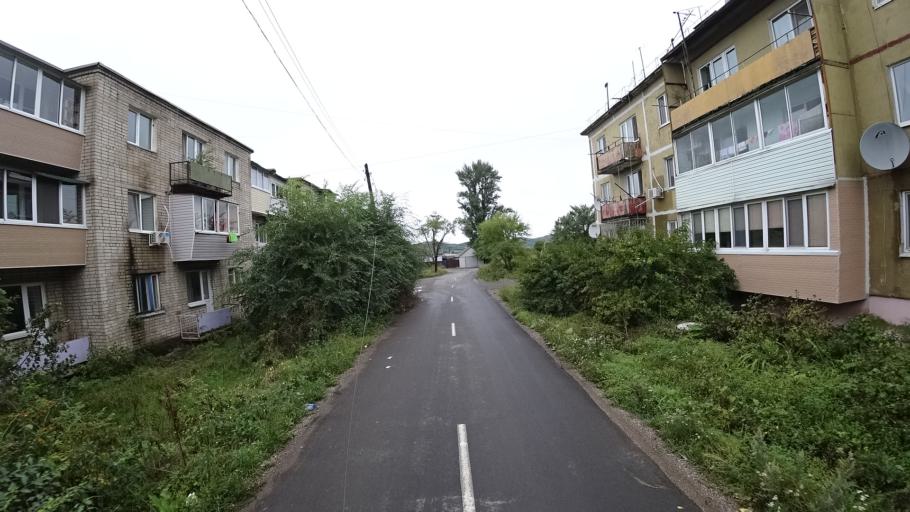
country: RU
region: Primorskiy
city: Monastyrishche
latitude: 44.2005
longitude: 132.4962
